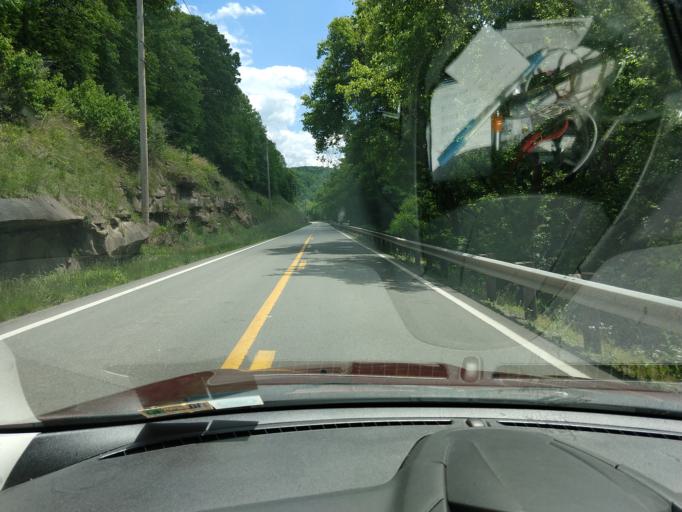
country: US
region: West Virginia
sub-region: Gilmer County
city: Glenville
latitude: 38.8788
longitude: -80.7115
